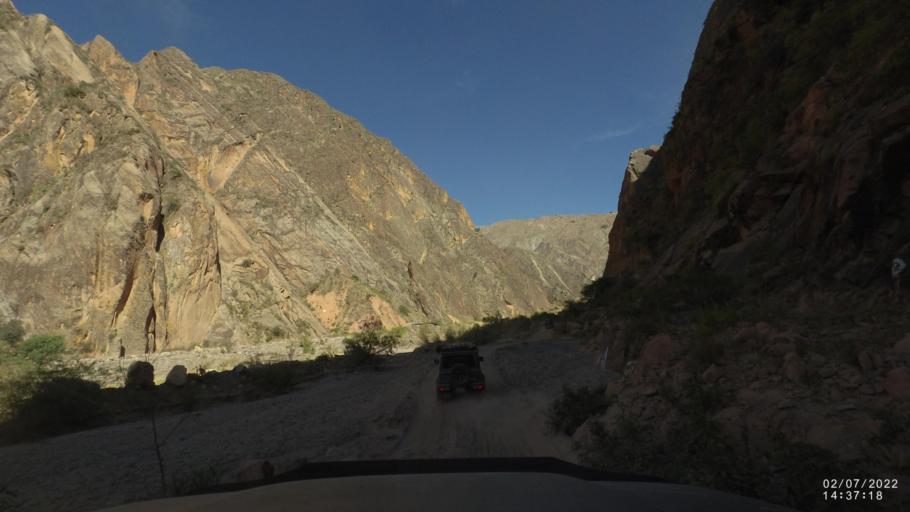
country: BO
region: Cochabamba
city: Irpa Irpa
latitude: -17.8416
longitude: -66.4188
